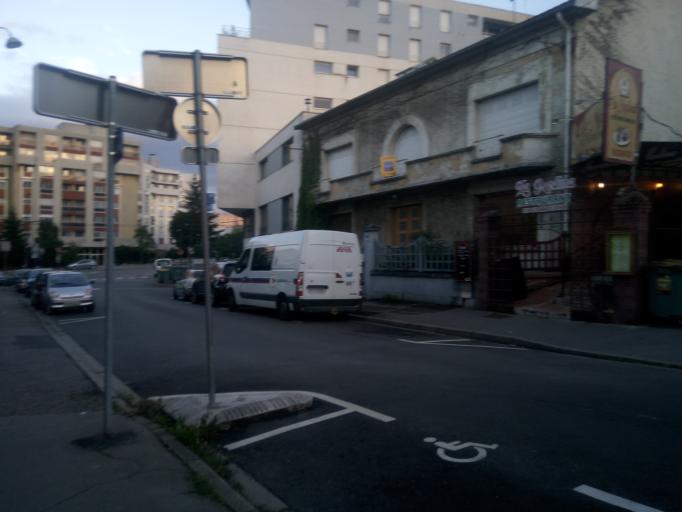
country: FR
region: Lorraine
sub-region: Departement de Meurthe-et-Moselle
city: Villers-les-Nancy
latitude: 48.6677
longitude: 6.1666
